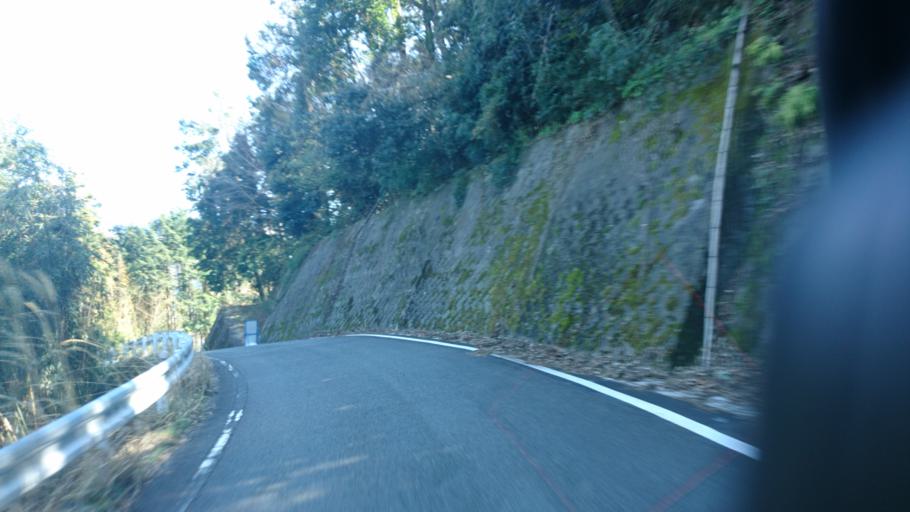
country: JP
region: Shizuoka
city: Fujinomiya
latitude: 35.3279
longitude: 138.4400
